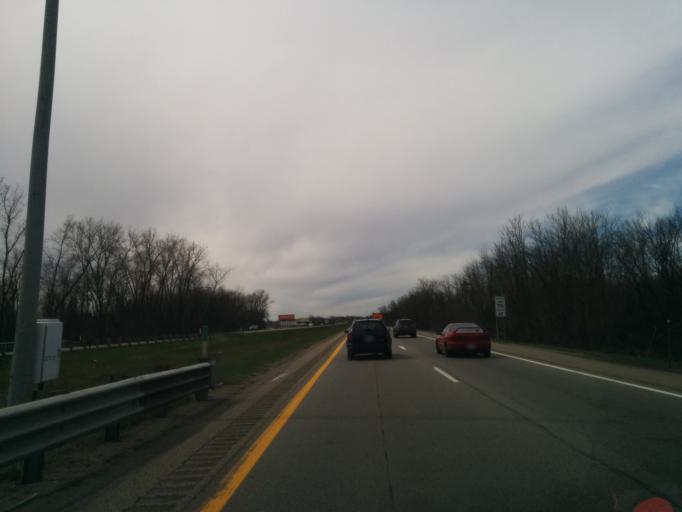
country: US
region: Michigan
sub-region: Kent County
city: Grandville
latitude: 42.9276
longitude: -85.7445
